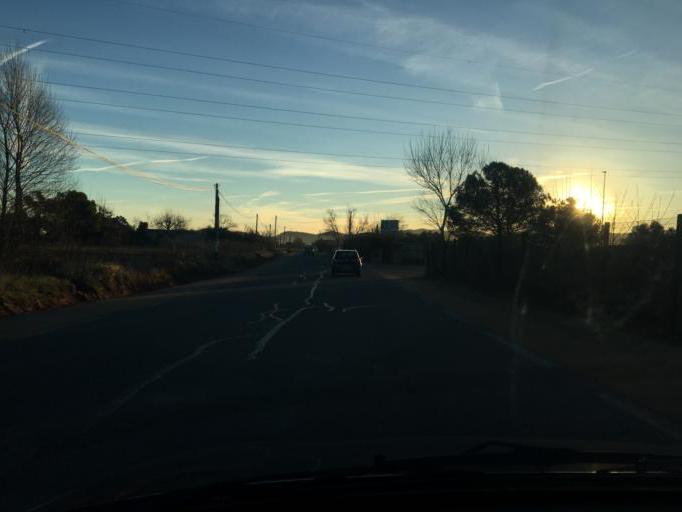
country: FR
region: Provence-Alpes-Cote d'Azur
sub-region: Departement du Var
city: Les Arcs
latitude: 43.4502
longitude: 6.4644
